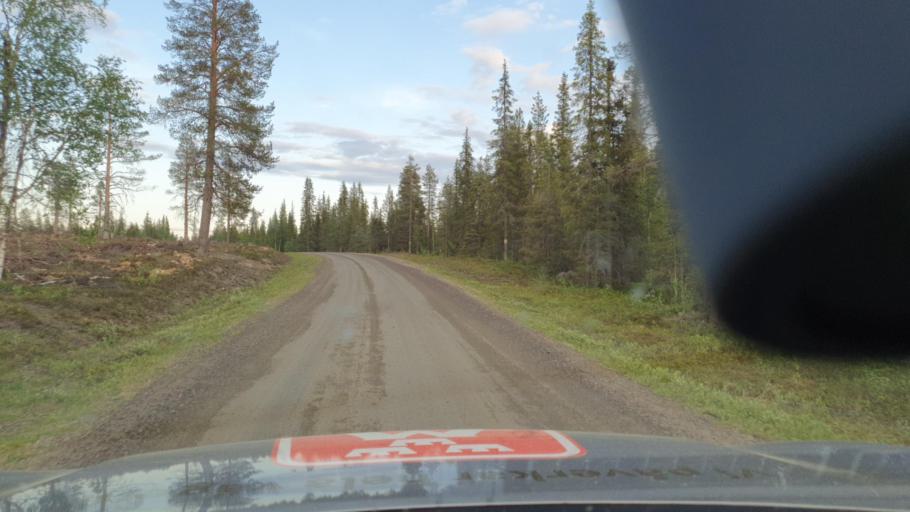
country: SE
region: Norrbotten
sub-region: Bodens Kommun
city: Boden
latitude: 66.5602
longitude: 21.4336
